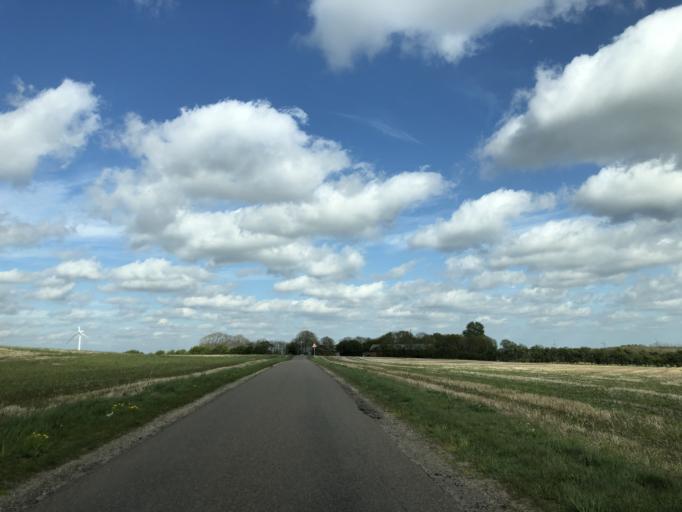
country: DK
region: Central Jutland
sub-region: Herning Kommune
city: Avlum
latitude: 56.3063
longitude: 8.7475
